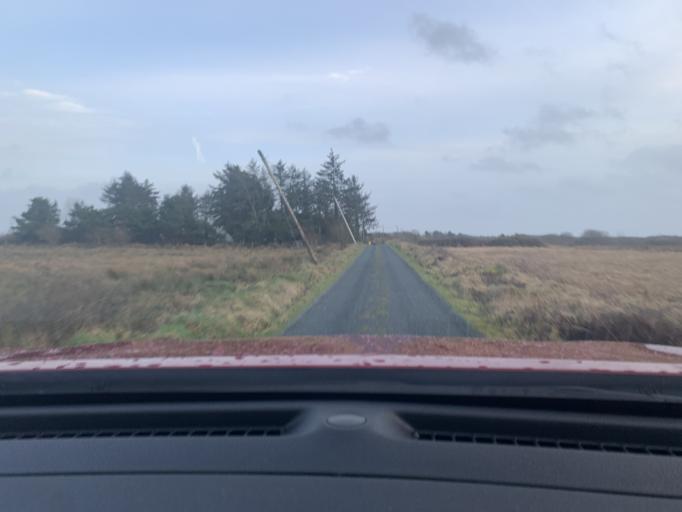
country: IE
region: Connaught
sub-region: Roscommon
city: Ballaghaderreen
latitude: 53.9574
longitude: -8.5350
